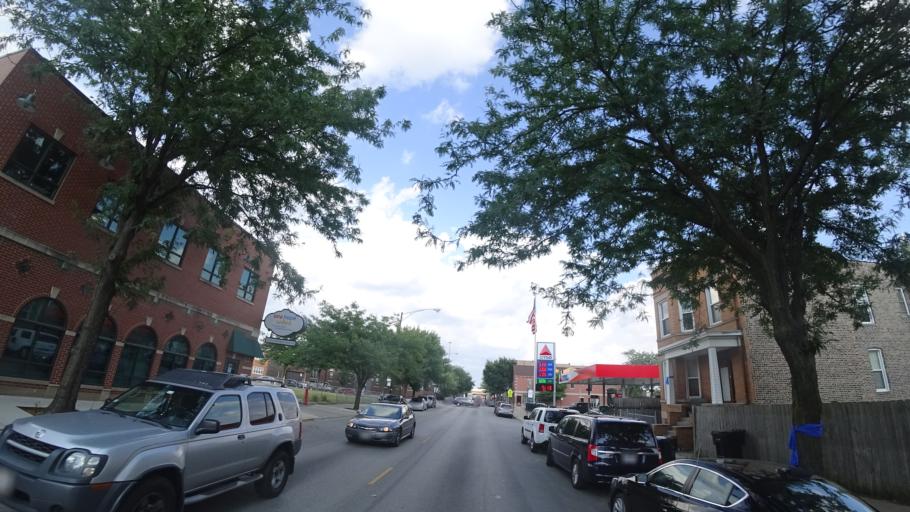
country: US
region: Illinois
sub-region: Cook County
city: Chicago
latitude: 41.8381
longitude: -87.6399
